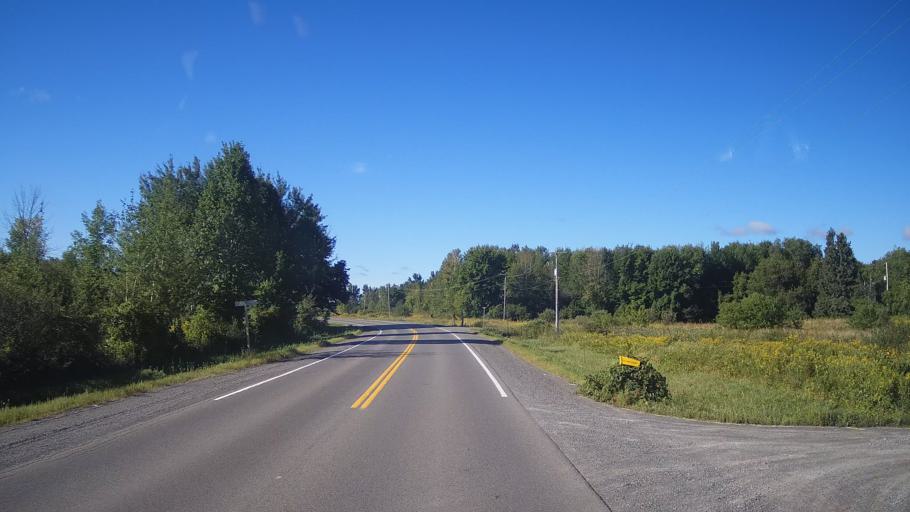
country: CA
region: Ontario
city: Bells Corners
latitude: 45.0874
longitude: -75.6303
